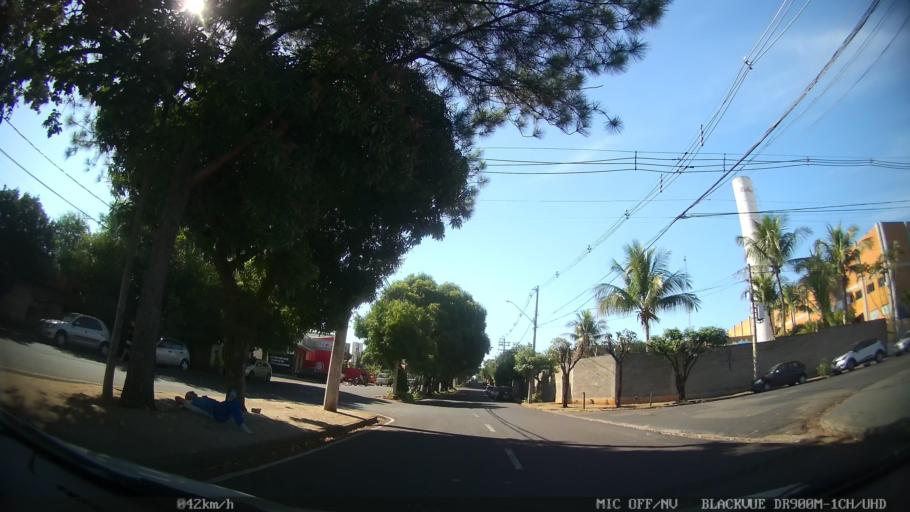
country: BR
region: Sao Paulo
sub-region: Sao Jose Do Rio Preto
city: Sao Jose do Rio Preto
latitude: -20.8125
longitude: -49.4269
